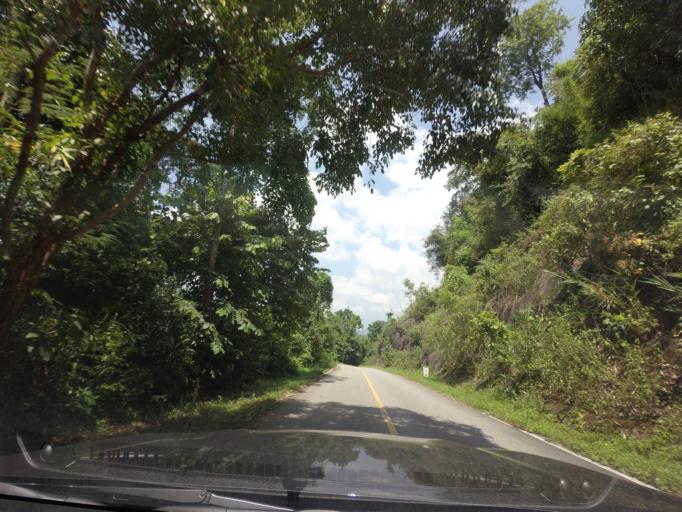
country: TH
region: Loei
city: Na Haeo
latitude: 17.6343
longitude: 100.9050
